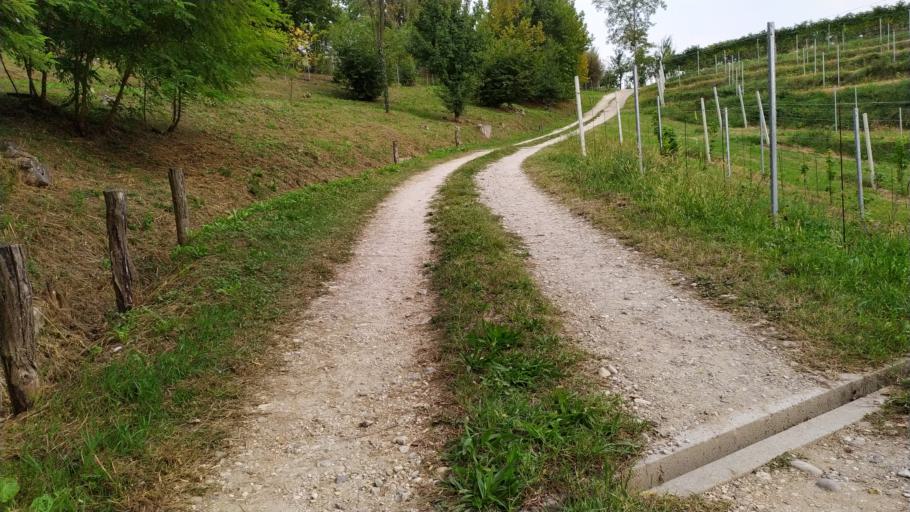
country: IT
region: Veneto
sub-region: Provincia di Treviso
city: Carpesica
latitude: 45.9194
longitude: 12.2919
